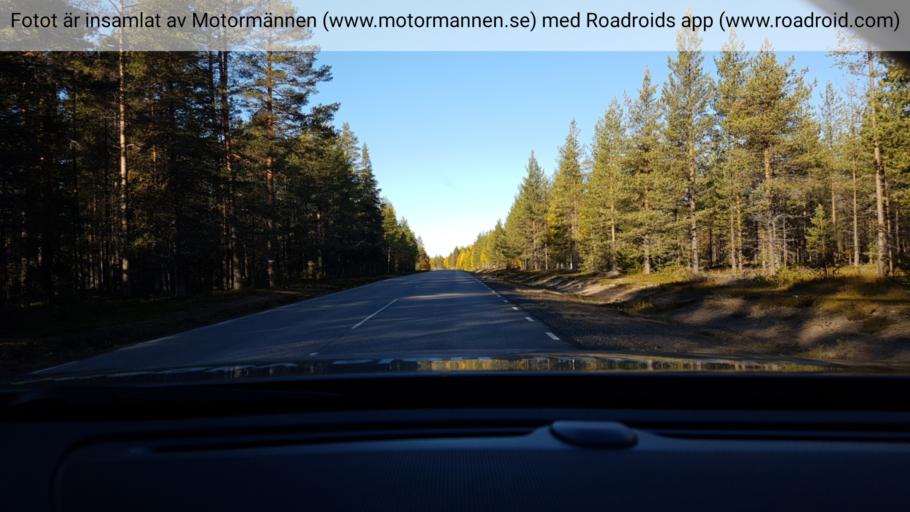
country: SE
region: Vaesterbotten
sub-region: Skelleftea Kommun
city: Storvik
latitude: 65.3354
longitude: 20.8866
